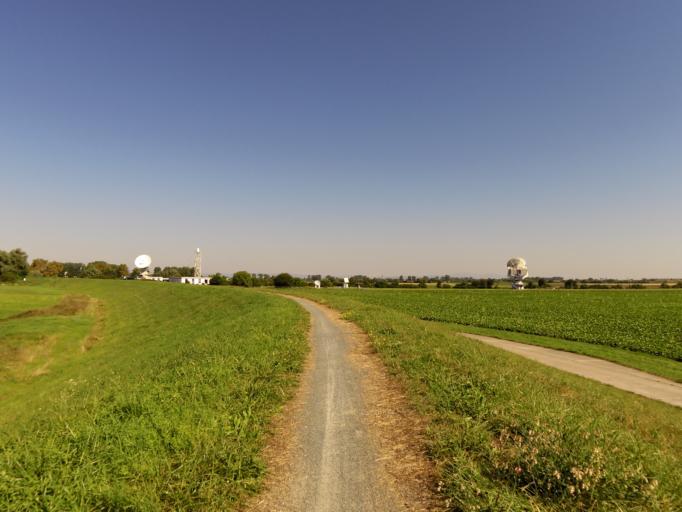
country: DE
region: Rheinland-Pfalz
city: Oppenheim
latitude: 49.8509
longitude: 8.3983
